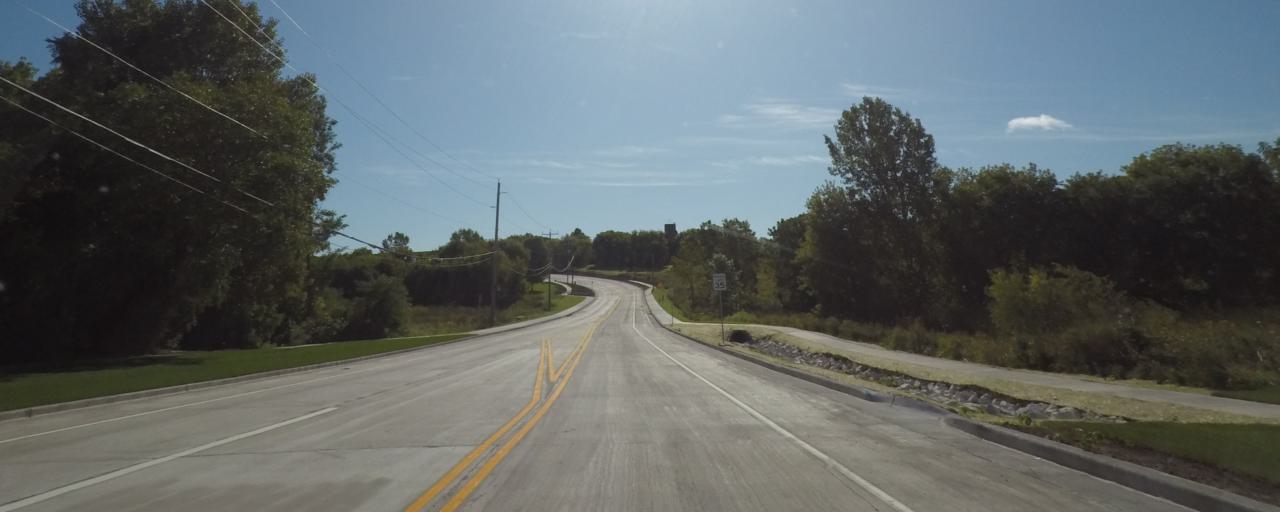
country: US
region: Wisconsin
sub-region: Waukesha County
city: Pewaukee
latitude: 43.0331
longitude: -88.2784
